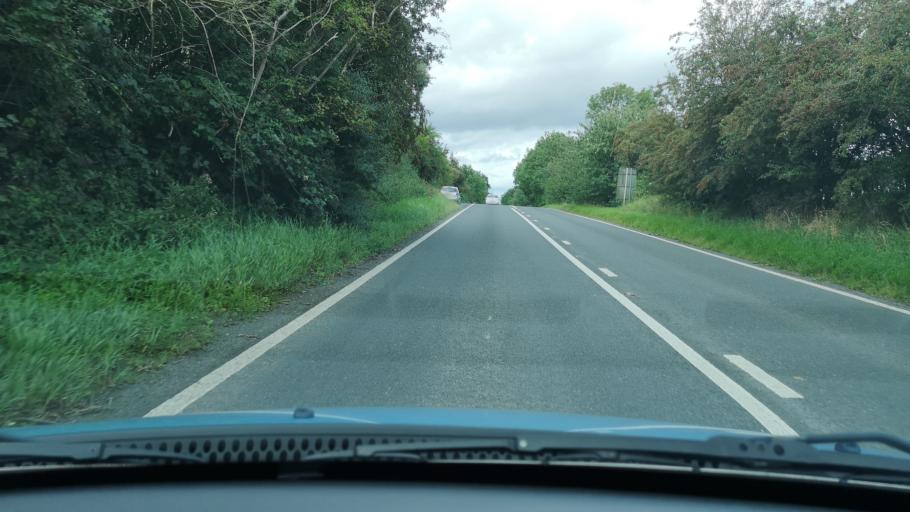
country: GB
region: England
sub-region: City and Borough of Wakefield
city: Badsworth
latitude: 53.6306
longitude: -1.3204
